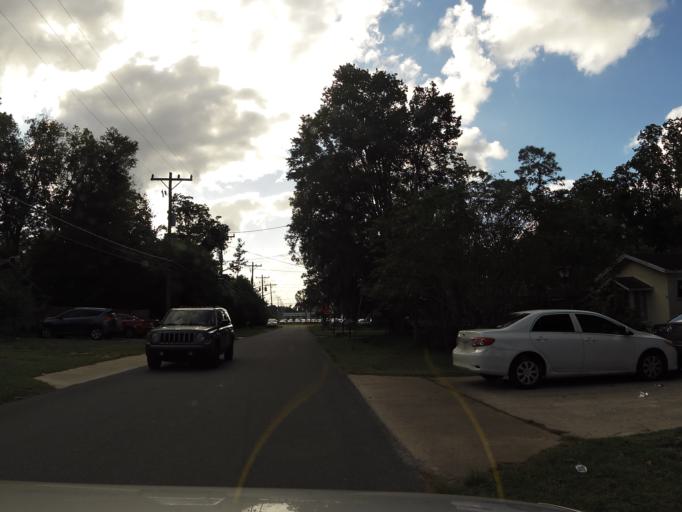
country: US
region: Florida
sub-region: Duval County
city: Jacksonville
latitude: 30.2893
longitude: -81.7288
